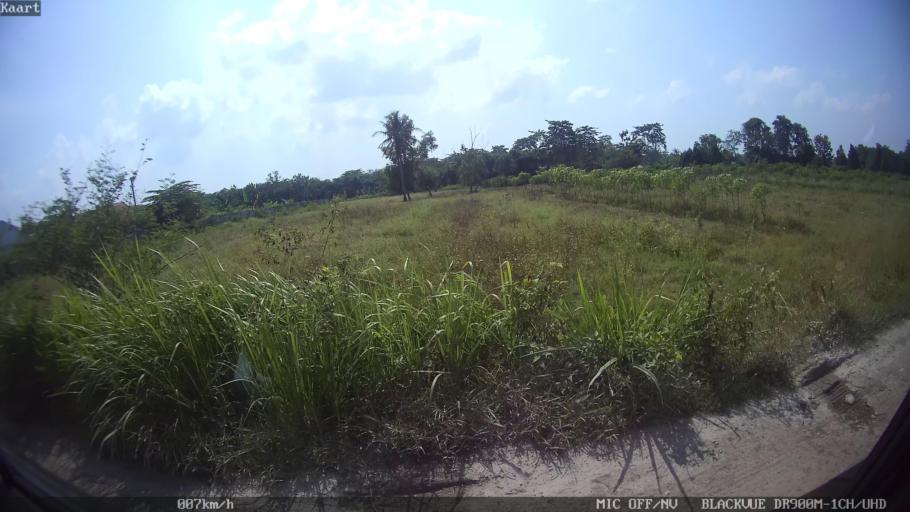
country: ID
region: Lampung
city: Natar
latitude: -5.2622
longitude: 105.1971
